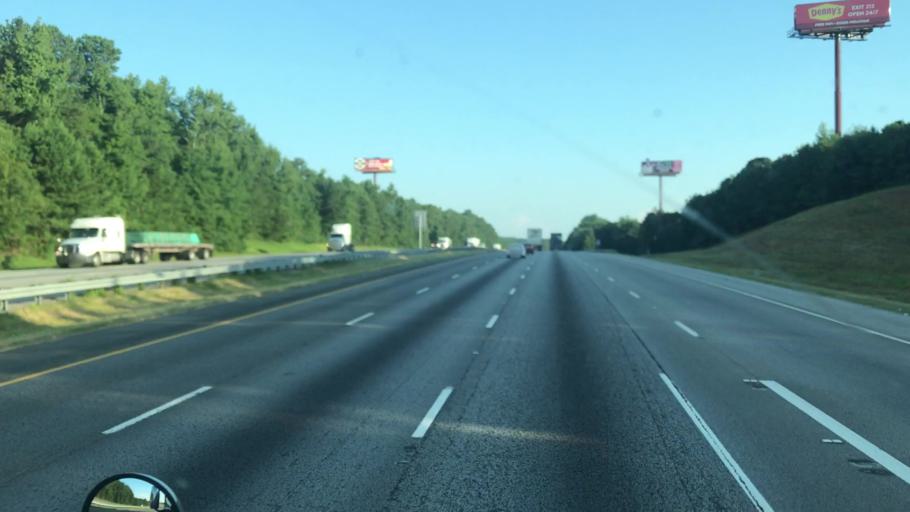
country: US
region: Georgia
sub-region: Henry County
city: Locust Grove
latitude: 33.2686
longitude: -84.1000
